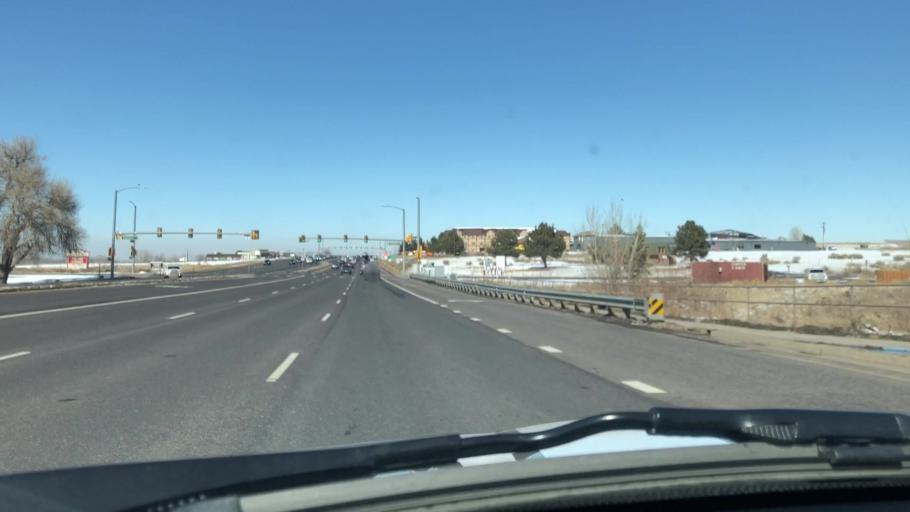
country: US
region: Colorado
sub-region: Douglas County
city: Parker
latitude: 39.5396
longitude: -104.7692
